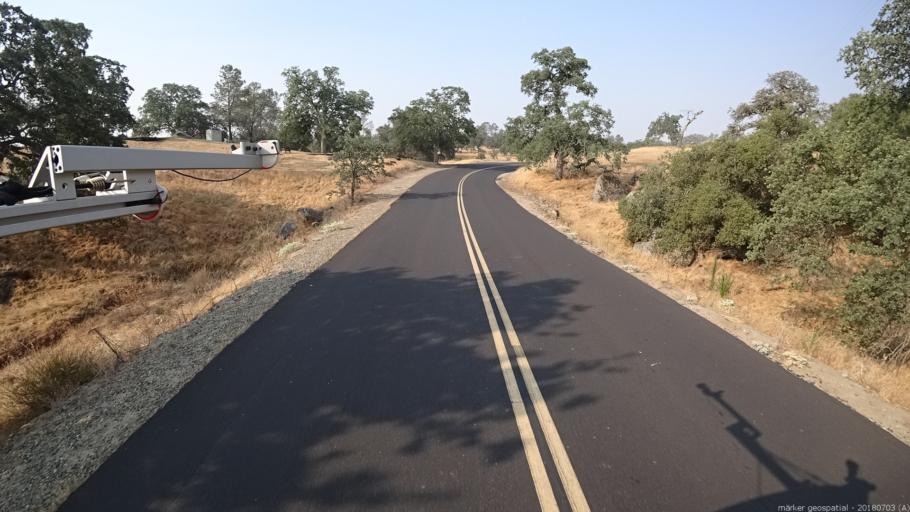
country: US
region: California
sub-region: Madera County
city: Yosemite Lakes
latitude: 37.0246
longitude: -119.6812
